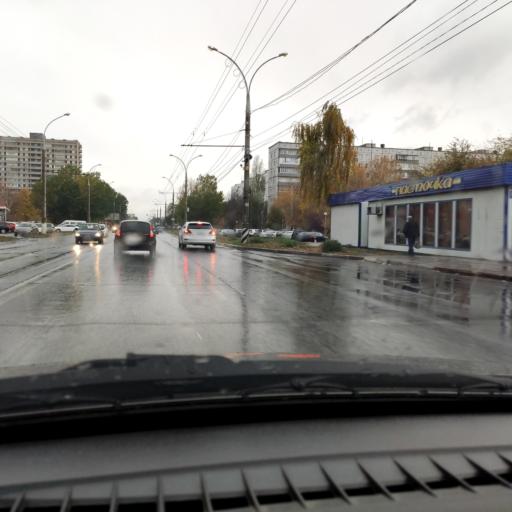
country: RU
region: Samara
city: Tol'yatti
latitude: 53.5062
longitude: 49.2823
